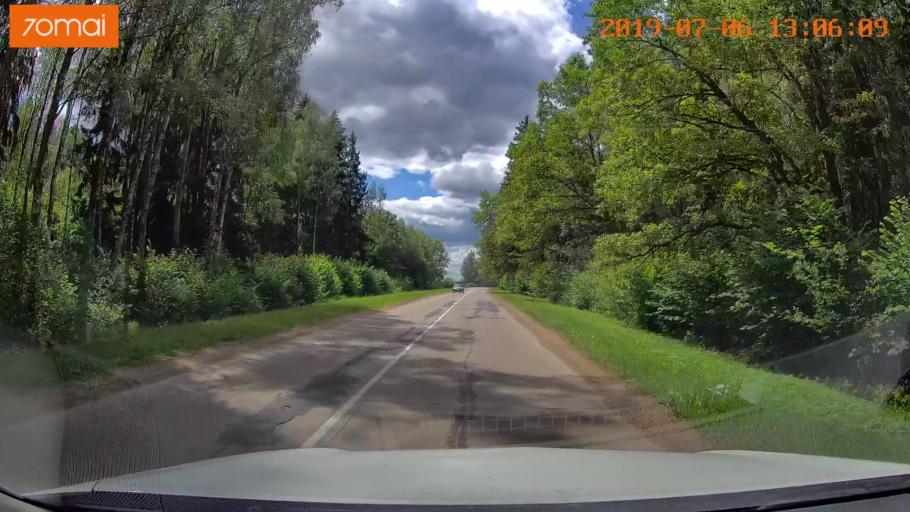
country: BY
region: Minsk
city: Dzyarzhynsk
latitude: 53.6836
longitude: 27.0573
